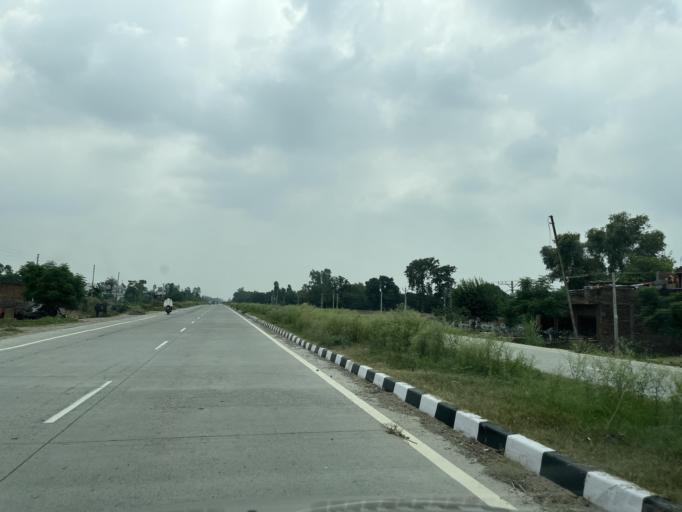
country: IN
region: Uttar Pradesh
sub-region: Bijnor
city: Najibabad
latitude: 29.5491
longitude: 78.3395
